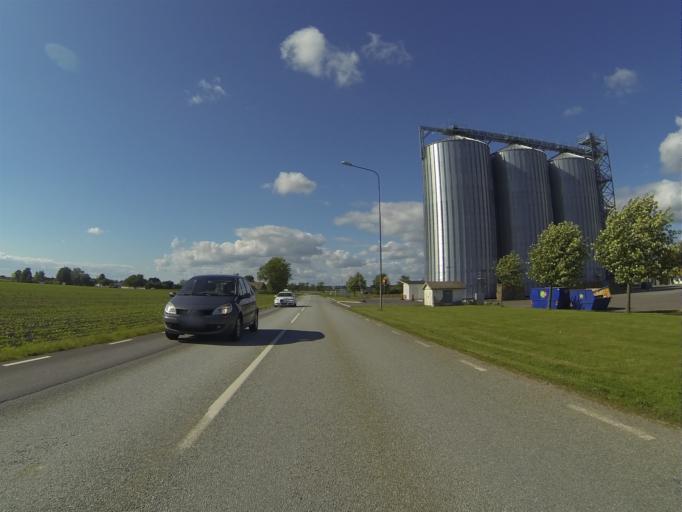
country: SE
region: Skane
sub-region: Staffanstorps Kommun
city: Staffanstorp
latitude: 55.6697
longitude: 13.1874
